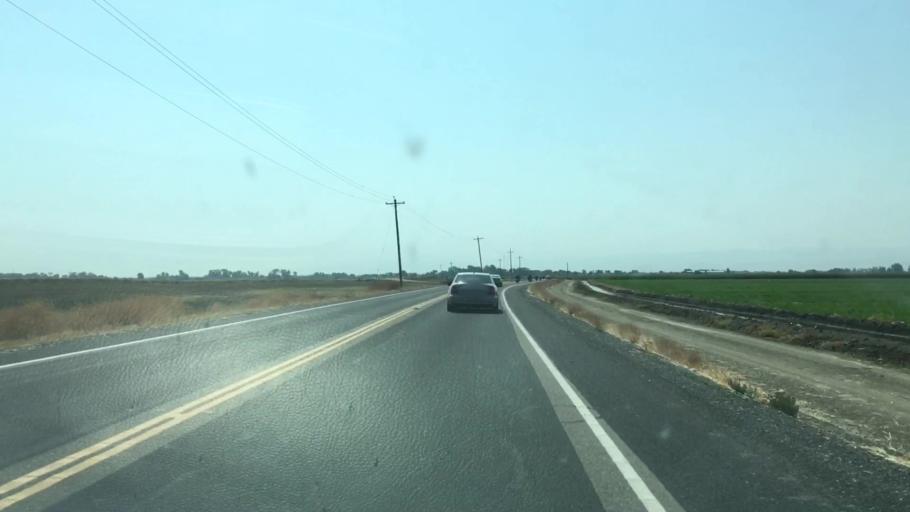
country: US
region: California
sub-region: San Joaquin County
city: Tracy
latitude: 37.8382
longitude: -121.4515
